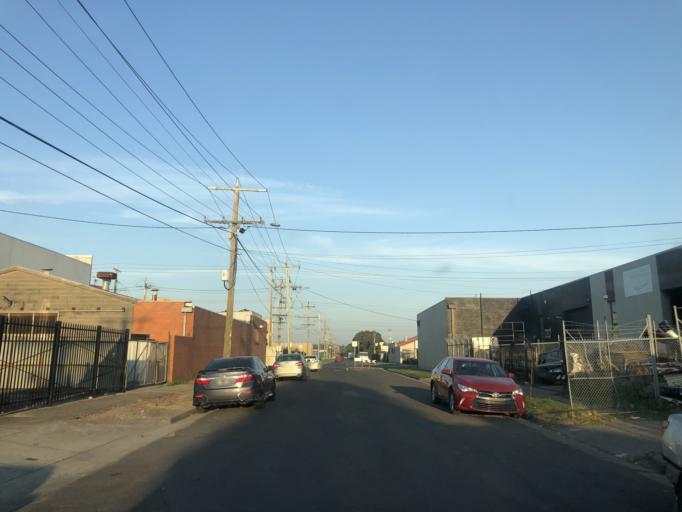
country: AU
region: Victoria
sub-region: Casey
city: Doveton
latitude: -37.9982
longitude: 145.2269
